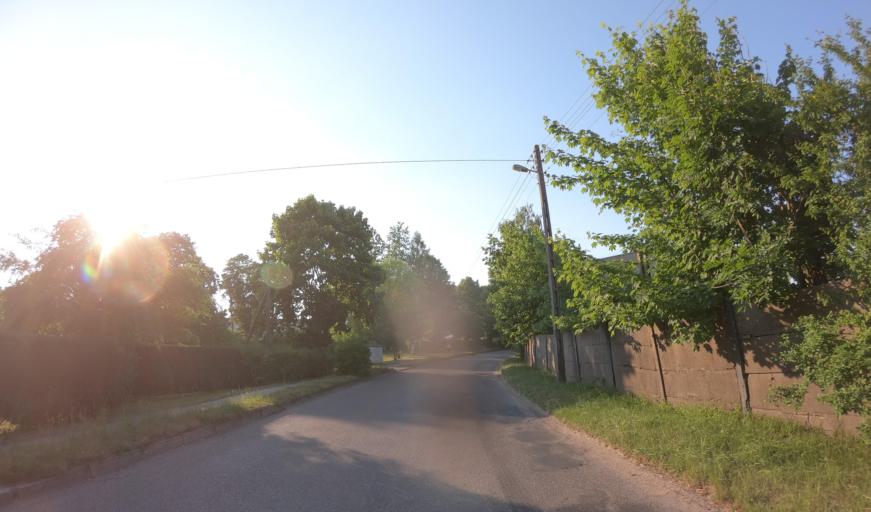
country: PL
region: West Pomeranian Voivodeship
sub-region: Powiat lobeski
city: Resko
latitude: 53.7659
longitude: 15.4039
